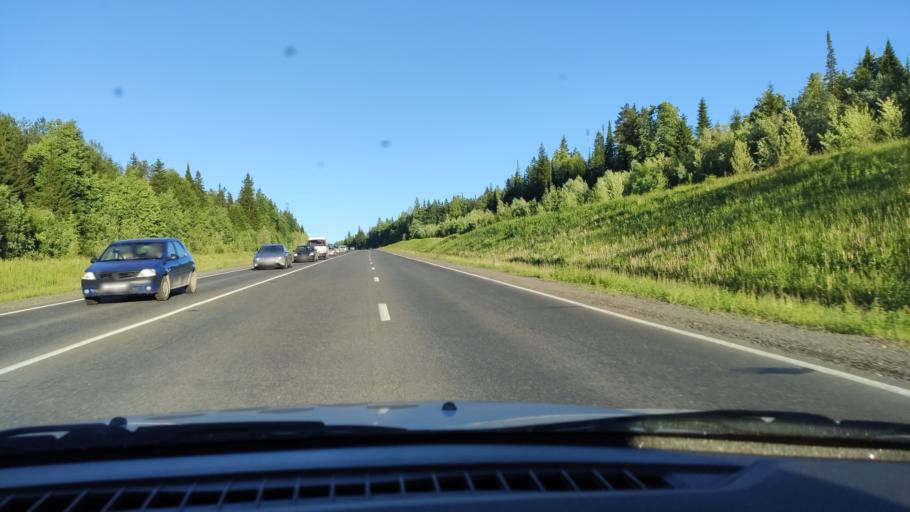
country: RU
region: Perm
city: Novyye Lyady
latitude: 58.0356
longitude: 56.4740
